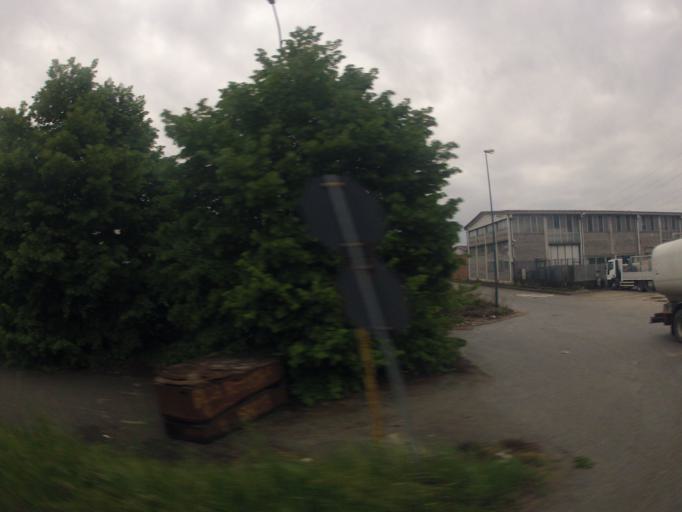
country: IT
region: Piedmont
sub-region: Provincia di Torino
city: Carignano
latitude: 44.8865
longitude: 7.6680
